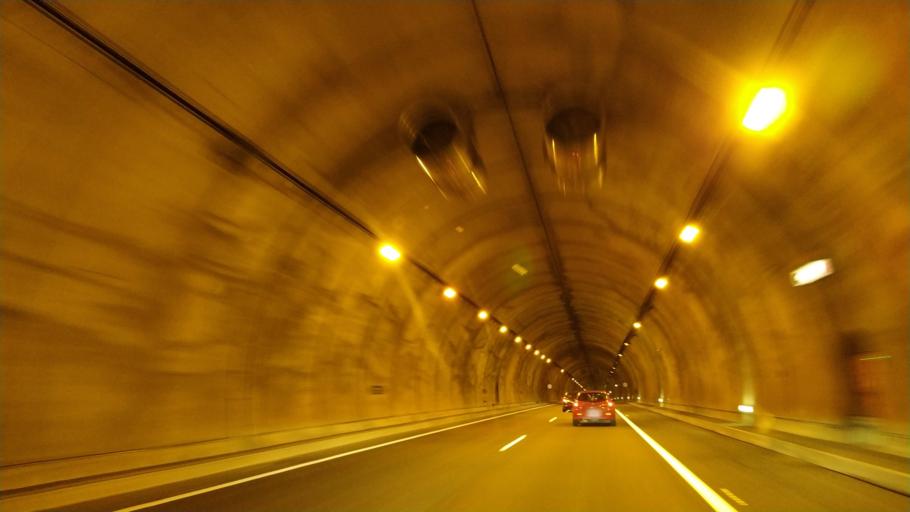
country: ES
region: Cantabria
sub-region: Provincia de Cantabria
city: Arenas de Iguna
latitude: 43.2057
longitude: -4.0738
